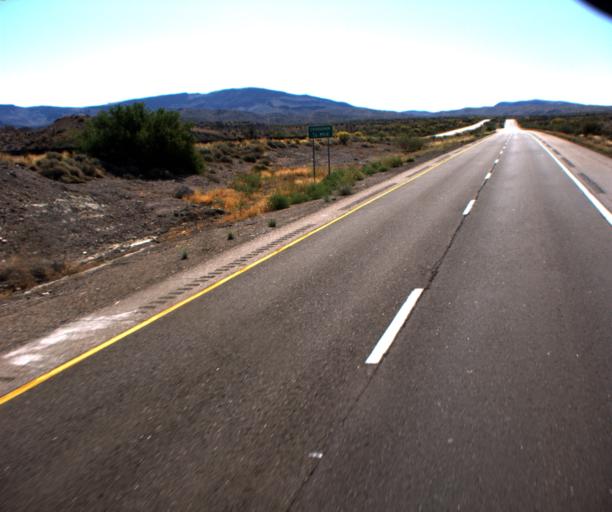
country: US
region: Arizona
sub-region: Yavapai County
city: Bagdad
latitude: 34.6346
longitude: -113.5530
